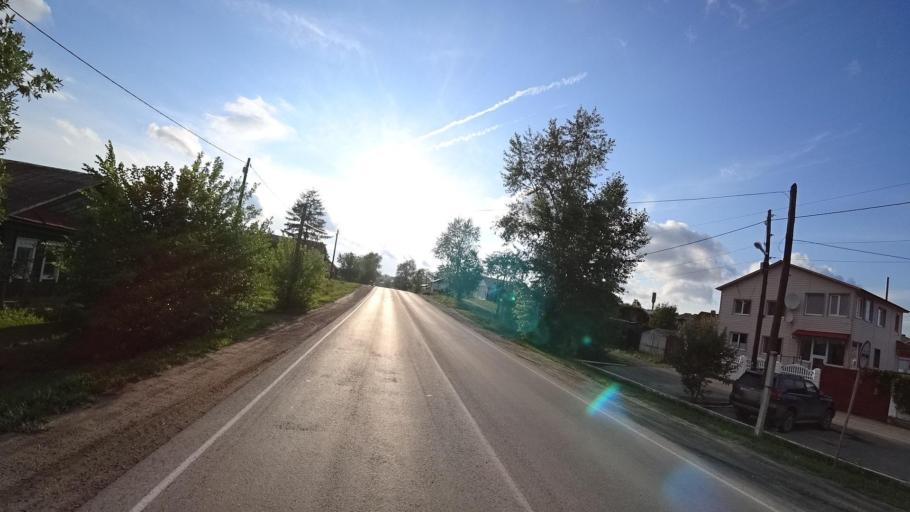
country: RU
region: Sverdlovsk
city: Kamyshlov
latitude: 56.8466
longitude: 62.6777
